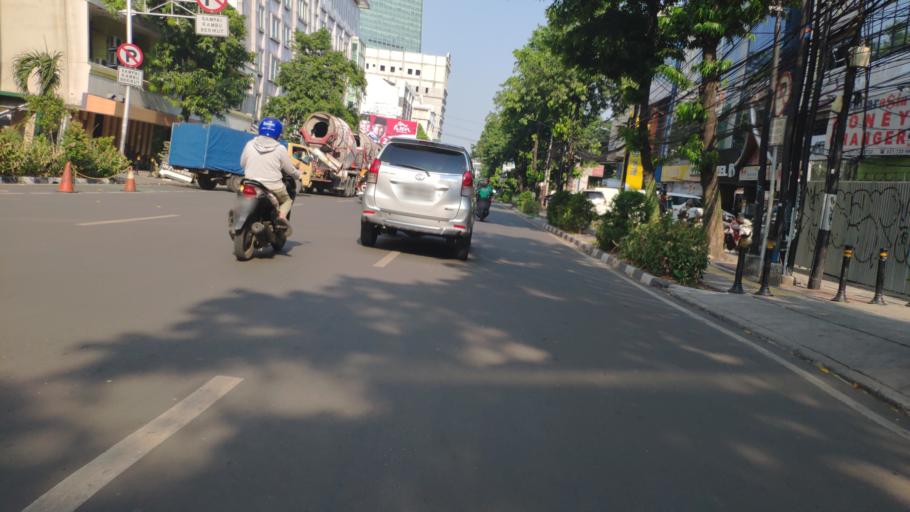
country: ID
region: Jakarta Raya
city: Jakarta
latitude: -6.2459
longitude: 106.7991
